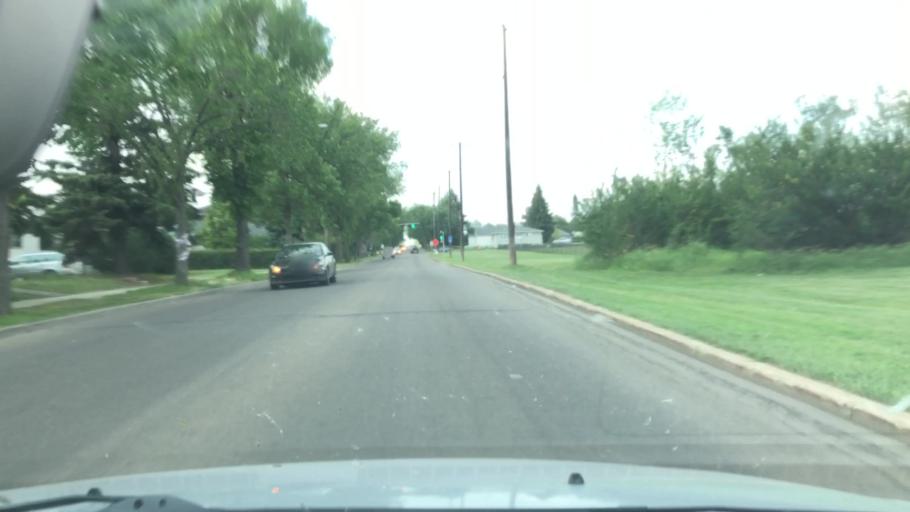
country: CA
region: Alberta
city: Edmonton
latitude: 53.5857
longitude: -113.5166
